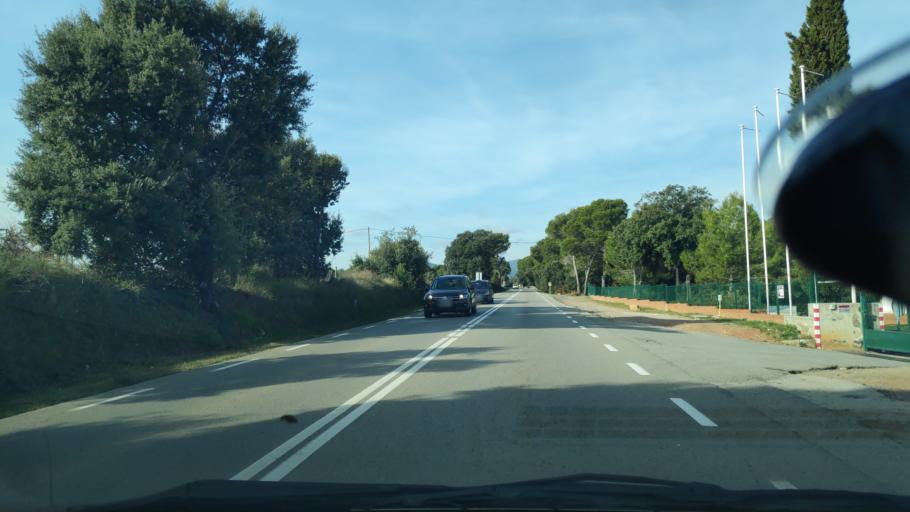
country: ES
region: Catalonia
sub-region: Provincia de Barcelona
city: Matadepera
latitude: 41.5892
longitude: 2.0470
